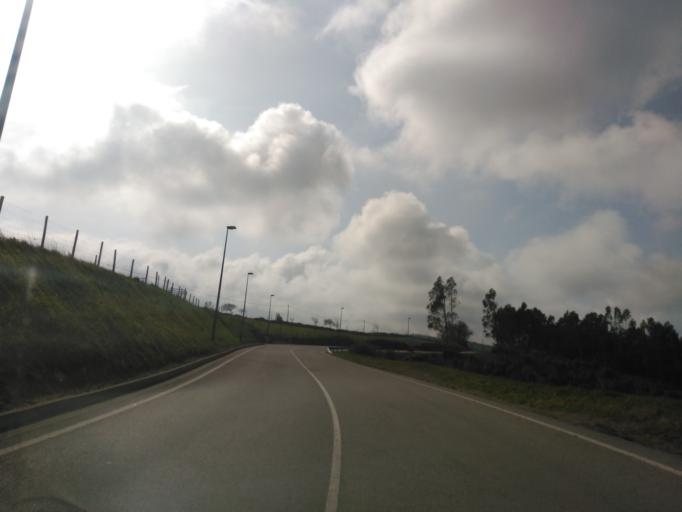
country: ES
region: Cantabria
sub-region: Provincia de Cantabria
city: Suances
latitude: 43.4215
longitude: -4.0629
